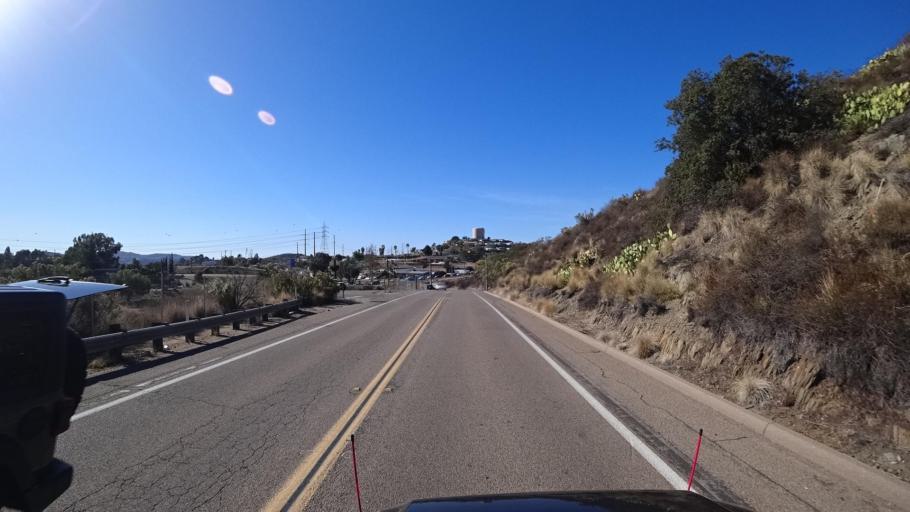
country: US
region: California
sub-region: San Diego County
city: Crest
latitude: 32.8459
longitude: -116.8808
